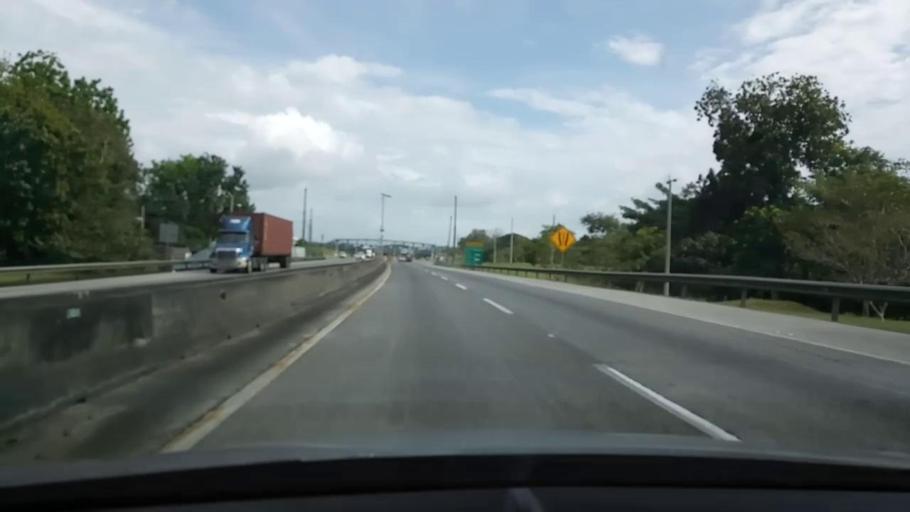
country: PA
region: Colon
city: Buena Vista
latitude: 9.2648
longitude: -79.7034
